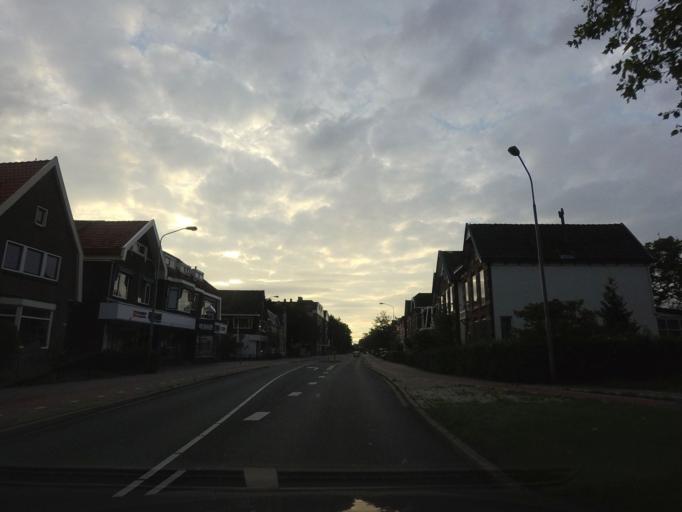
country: NL
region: North Holland
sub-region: Gemeente Zaanstad
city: Zaanstad
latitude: 52.4881
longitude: 4.7976
